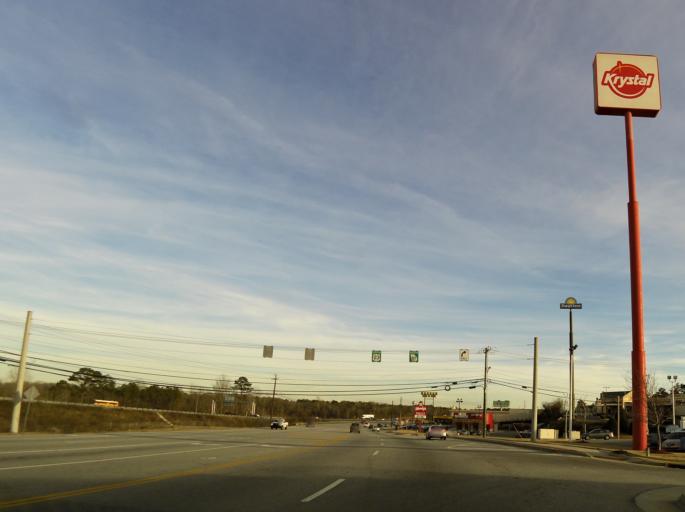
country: US
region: Georgia
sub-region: Bibb County
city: Macon
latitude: 32.9006
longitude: -83.6865
